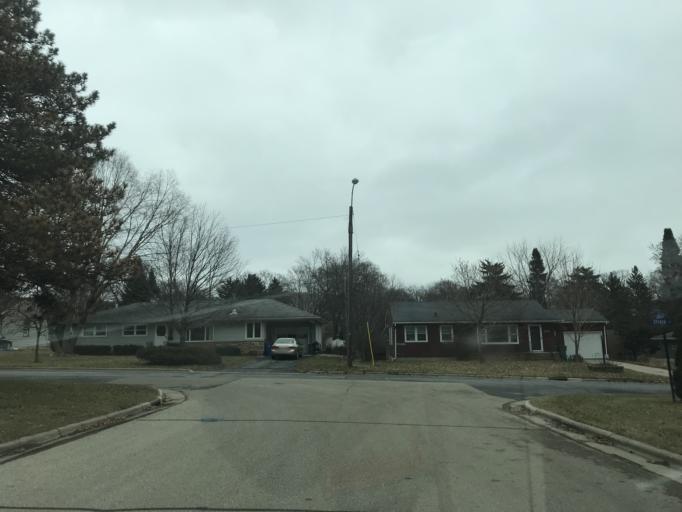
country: US
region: Wisconsin
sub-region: Dane County
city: Monona
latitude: 43.0538
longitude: -89.3300
